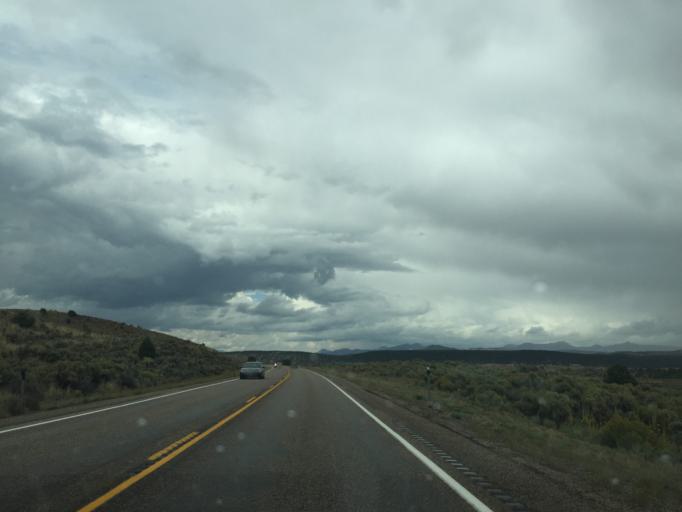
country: US
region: Utah
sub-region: Garfield County
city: Panguitch
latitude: 37.7310
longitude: -112.3803
